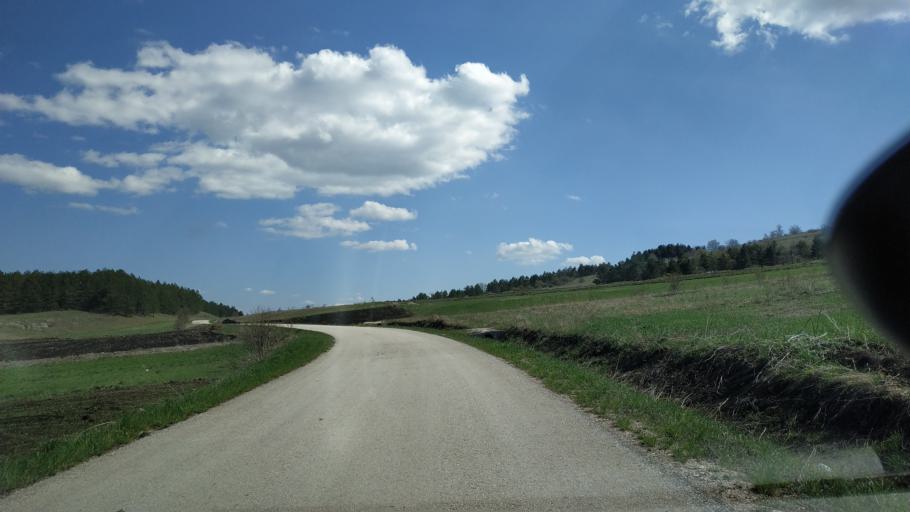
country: RS
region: Central Serbia
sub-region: Zajecarski Okrug
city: Soko Banja
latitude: 43.5943
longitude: 21.8844
